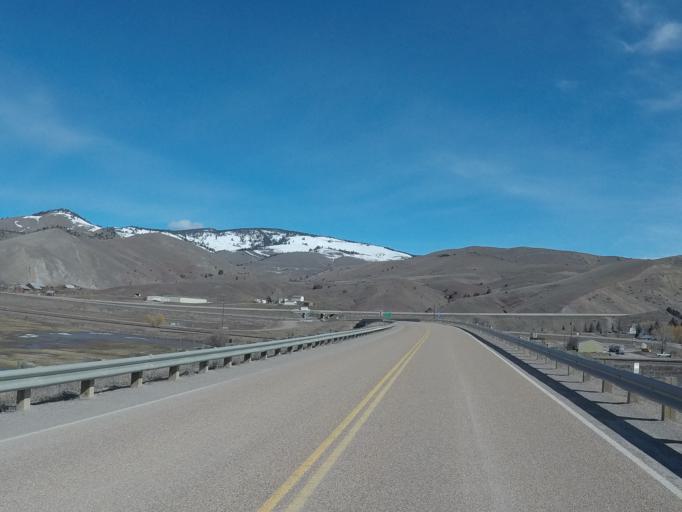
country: US
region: Montana
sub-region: Granite County
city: Philipsburg
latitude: 46.6678
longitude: -113.1542
